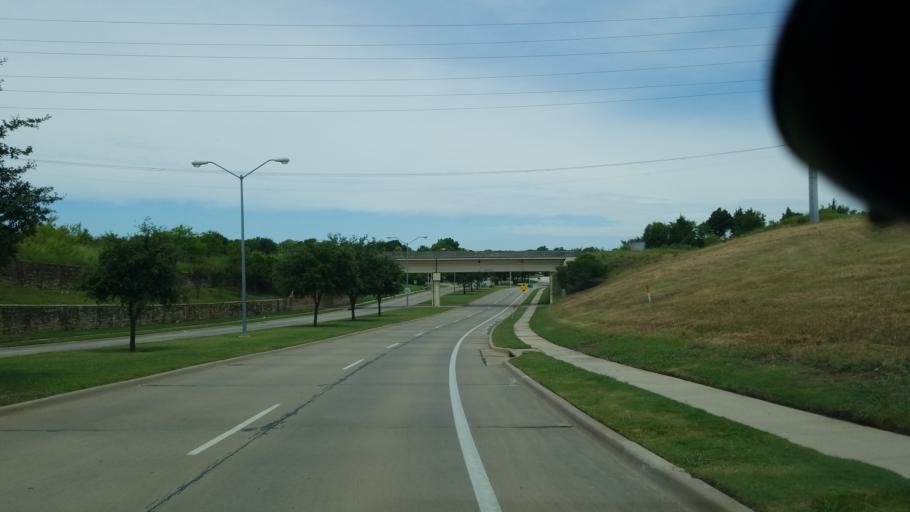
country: US
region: Texas
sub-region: Dallas County
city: Irving
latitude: 32.8448
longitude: -96.9343
